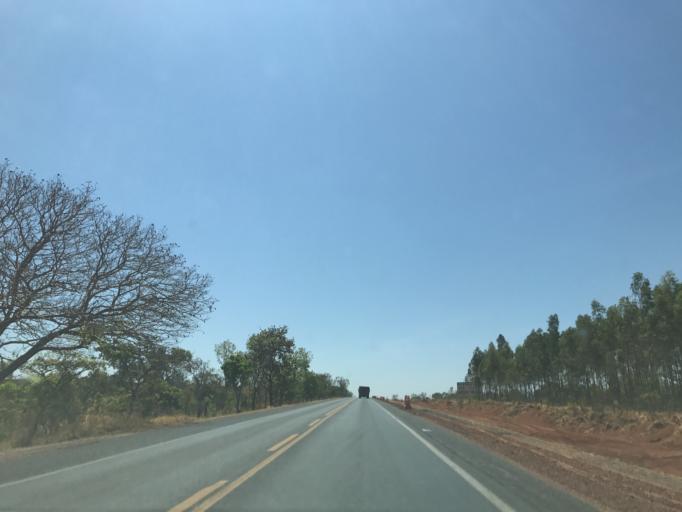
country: BR
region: Minas Gerais
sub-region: Prata
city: Prata
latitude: -19.3994
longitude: -48.8960
